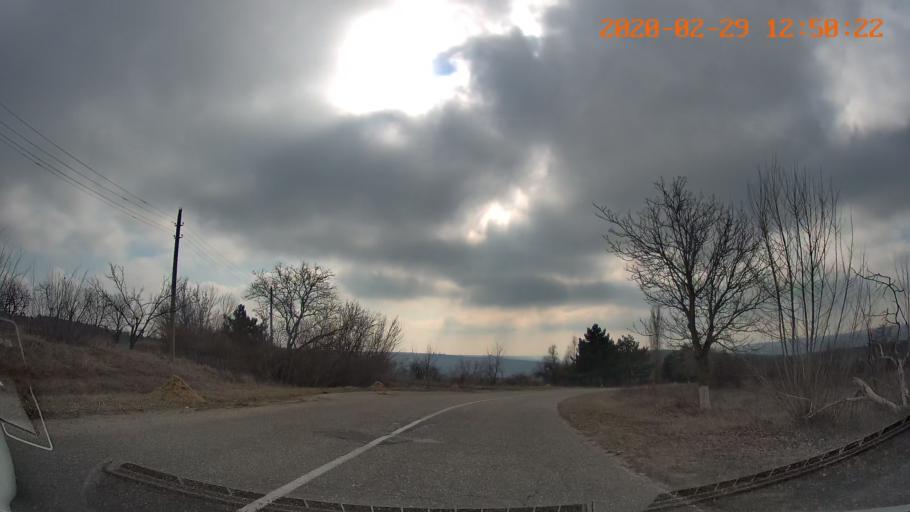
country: MD
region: Telenesti
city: Camenca
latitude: 48.1248
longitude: 28.7398
